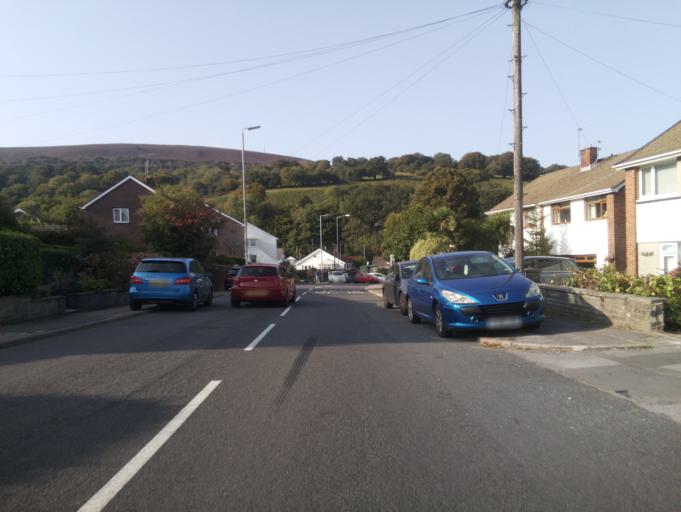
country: GB
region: Wales
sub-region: Torfaen County Borough
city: Cwmbran
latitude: 51.6648
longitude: -3.0461
